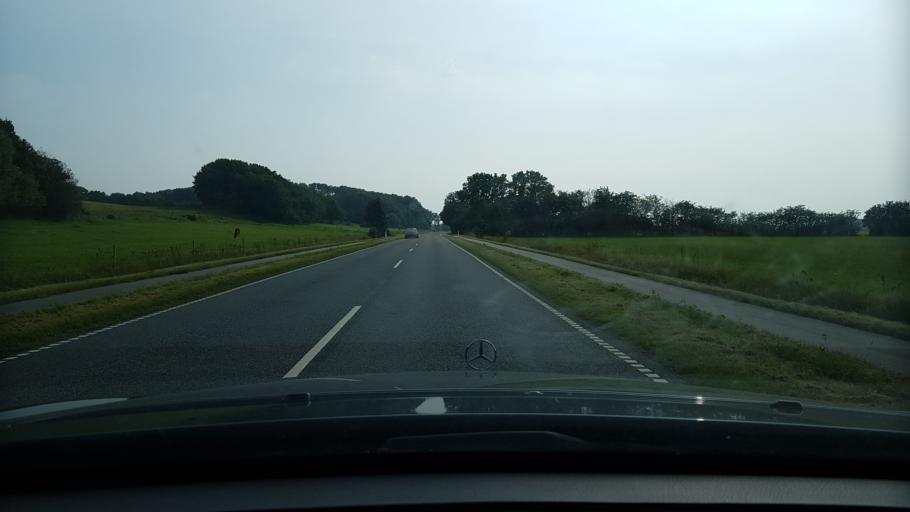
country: DK
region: North Denmark
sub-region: Alborg Kommune
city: Hals
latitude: 56.9180
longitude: 10.2586
